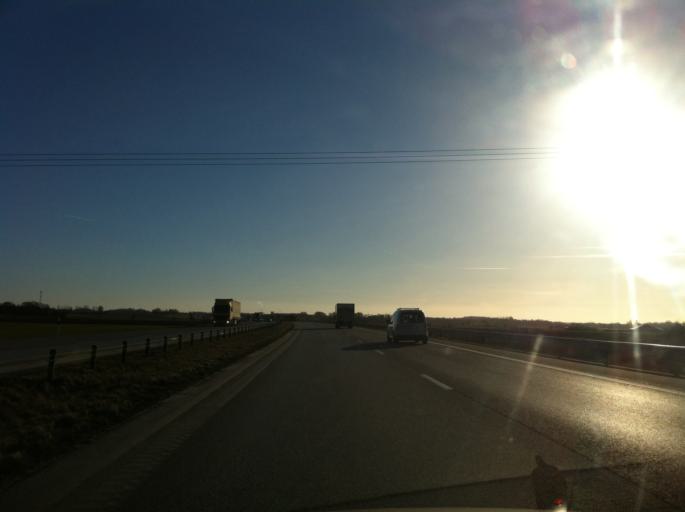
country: SE
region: Skane
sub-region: Angelholms Kommun
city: Strovelstorp
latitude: 56.1209
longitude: 12.8187
